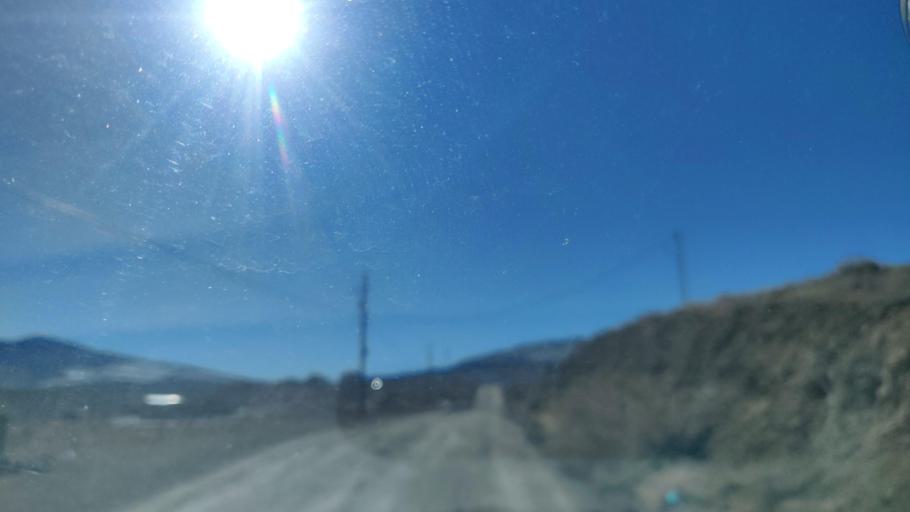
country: US
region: Colorado
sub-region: Mesa County
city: Palisade
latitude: 39.0893
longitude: -108.3296
